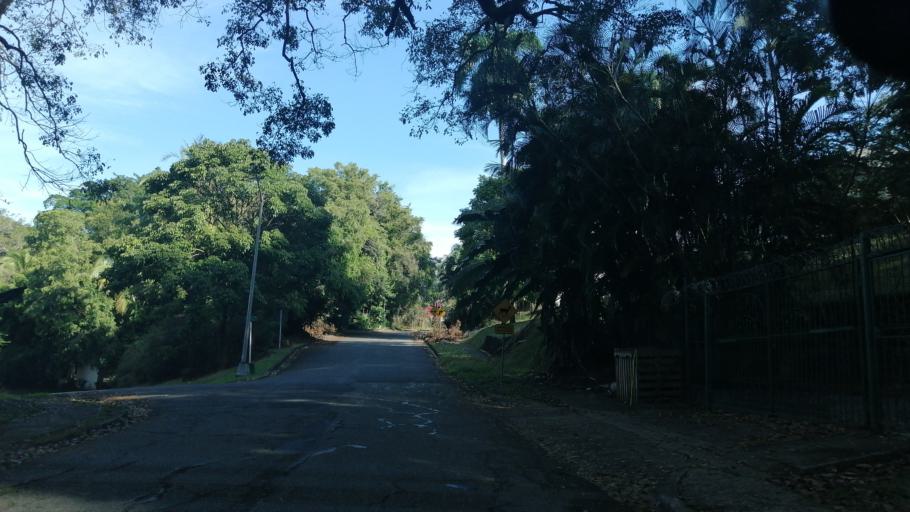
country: PA
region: Panama
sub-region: Distrito de Panama
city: Ancon
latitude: 8.9632
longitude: -79.5518
